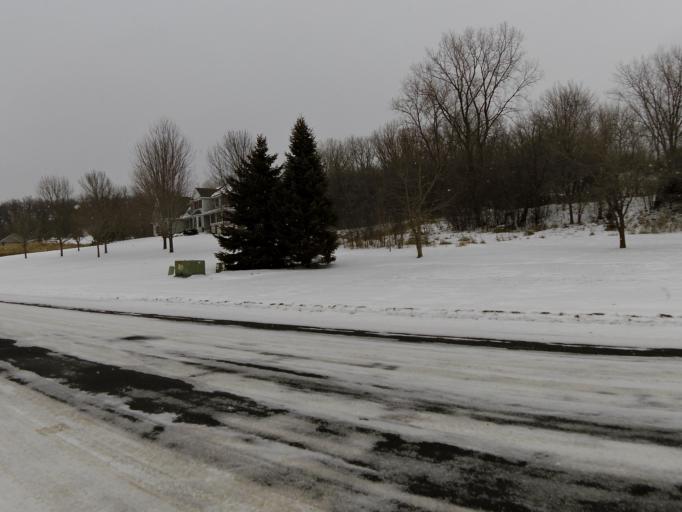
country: US
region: Minnesota
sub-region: Washington County
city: Lake Elmo
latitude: 44.9684
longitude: -92.8465
